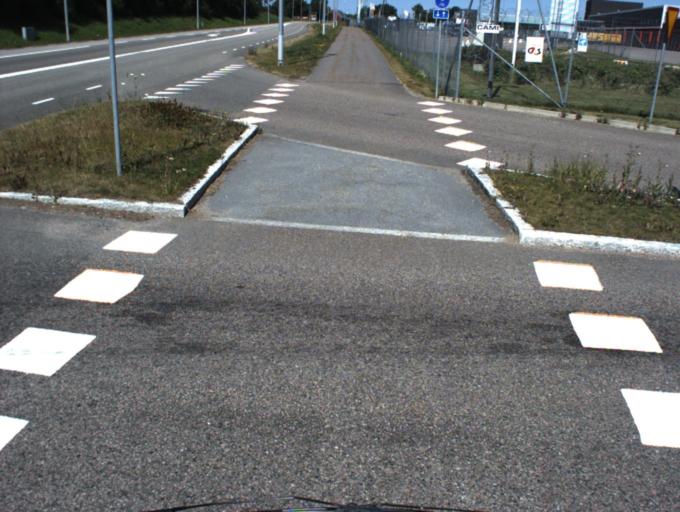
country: SE
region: Skane
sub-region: Helsingborg
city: Barslov
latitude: 56.0358
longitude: 12.7807
